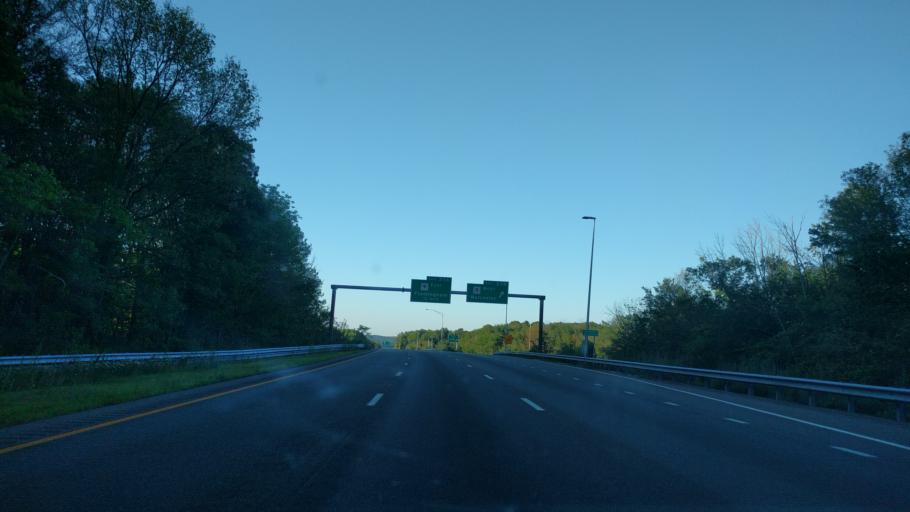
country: US
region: Massachusetts
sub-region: Worcester County
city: Southborough
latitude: 42.2929
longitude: -71.5682
